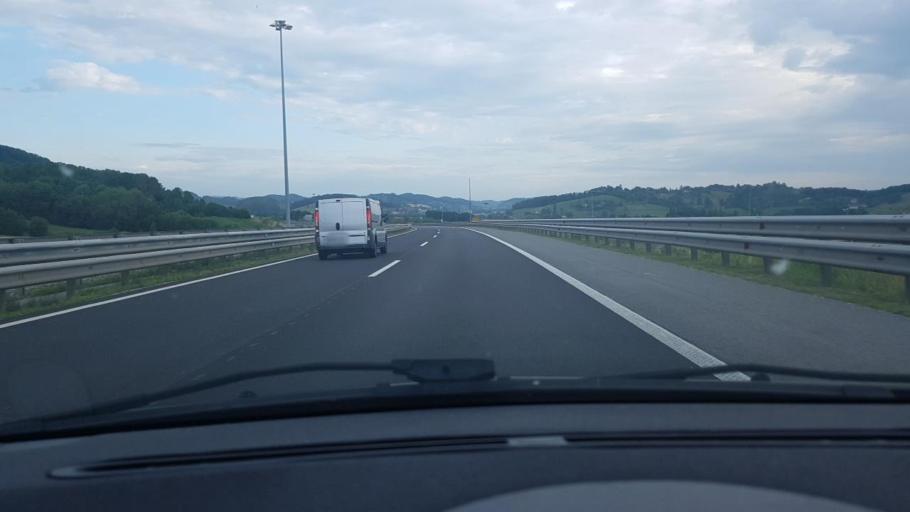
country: SI
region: Pesnica
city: Pesnica pri Mariboru
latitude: 46.5840
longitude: 15.6891
